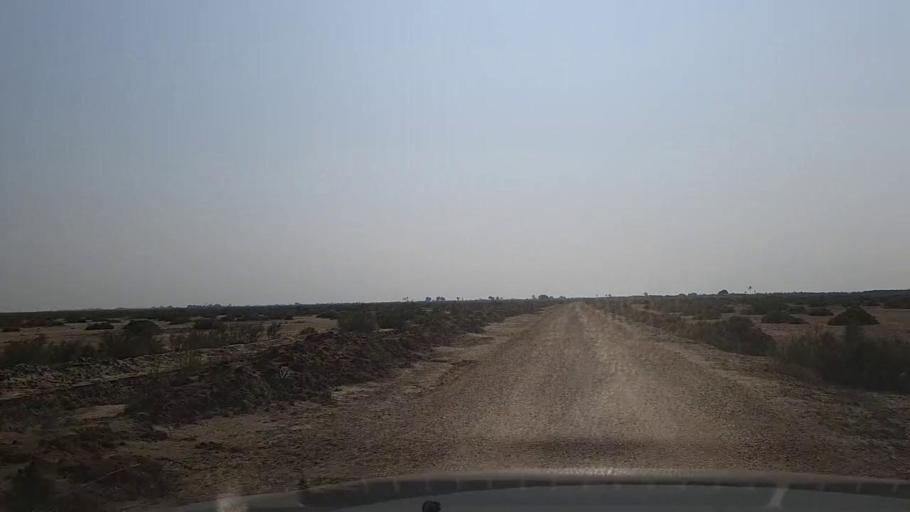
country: PK
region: Sindh
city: Mirpur Sakro
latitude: 24.4296
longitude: 67.7183
